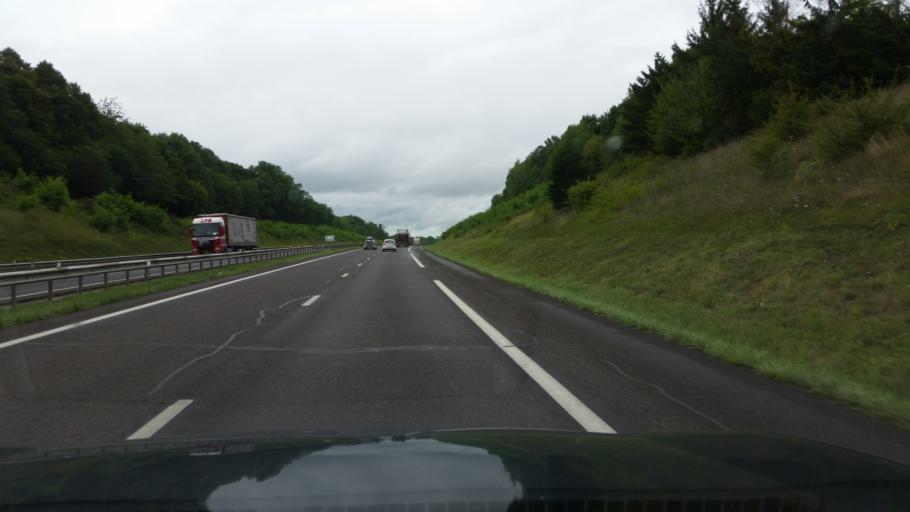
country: FR
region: Lorraine
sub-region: Departement de Meurthe-et-Moselle
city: Dommartin-les-Toul
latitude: 48.6366
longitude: 5.8812
